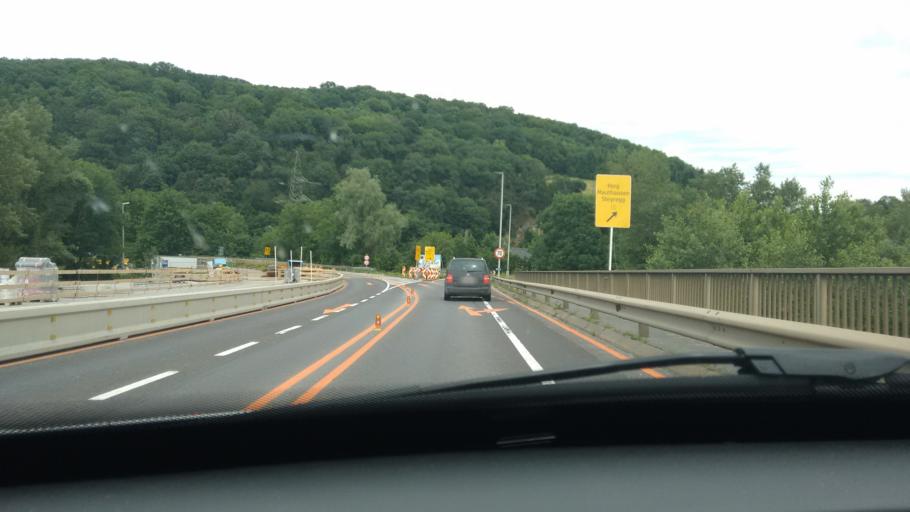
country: AT
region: Upper Austria
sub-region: Linz Stadt
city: Linz
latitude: 48.2851
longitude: 14.3247
